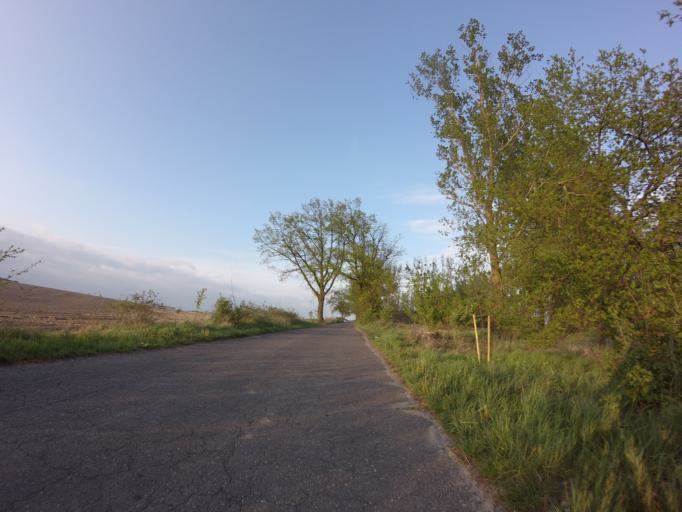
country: PL
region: West Pomeranian Voivodeship
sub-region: Powiat choszczenski
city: Choszczno
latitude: 53.1496
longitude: 15.3572
